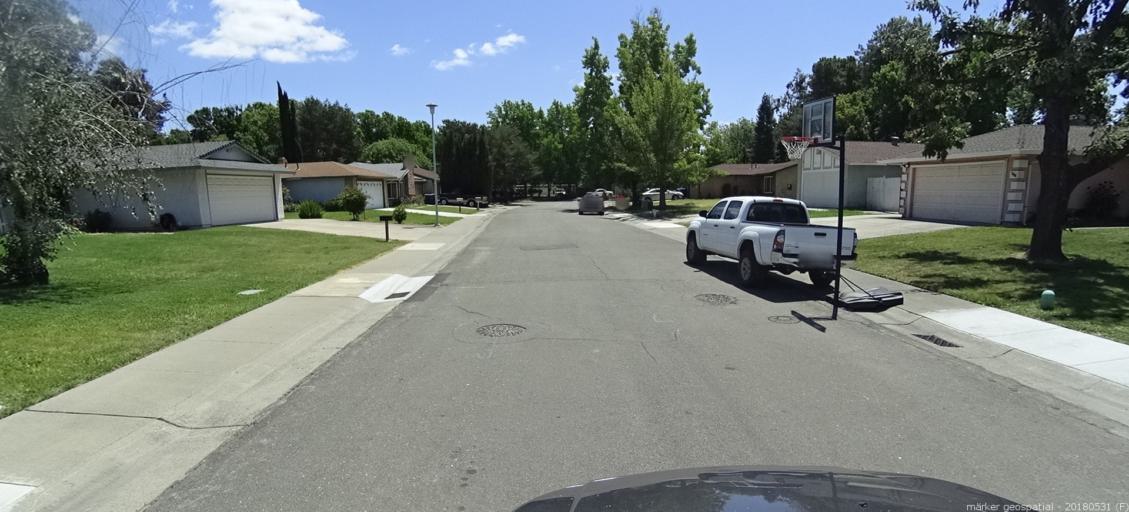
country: US
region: California
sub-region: Sacramento County
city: Sacramento
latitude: 38.6164
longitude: -121.5079
